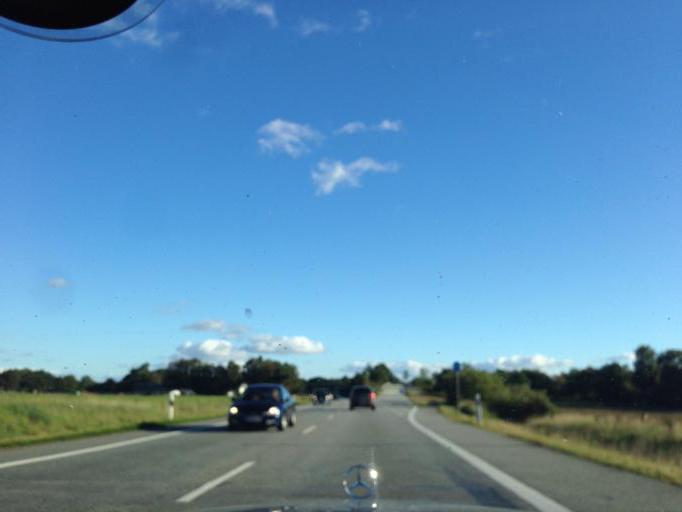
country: DE
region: Schleswig-Holstein
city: Rickling
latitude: 53.9892
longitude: 10.1870
